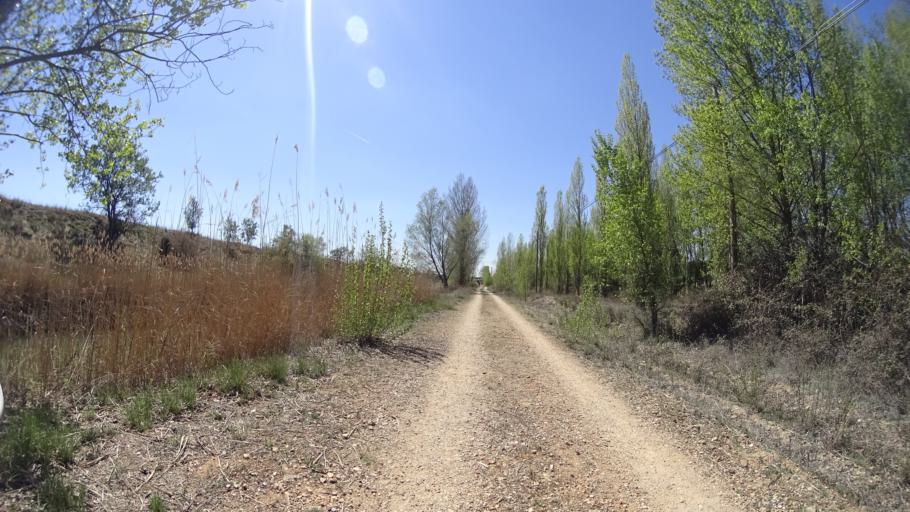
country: ES
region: Castille and Leon
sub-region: Provincia de Palencia
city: Duenas
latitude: 41.8595
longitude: -4.5499
